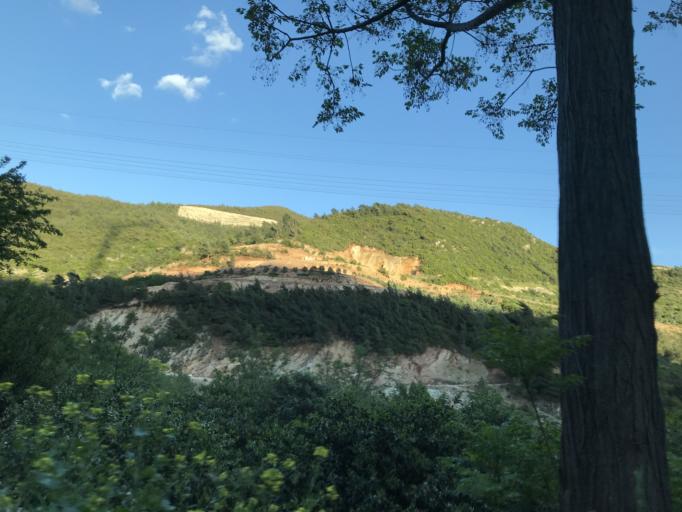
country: TR
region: Hatay
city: Buyukcat
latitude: 36.0843
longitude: 36.0509
